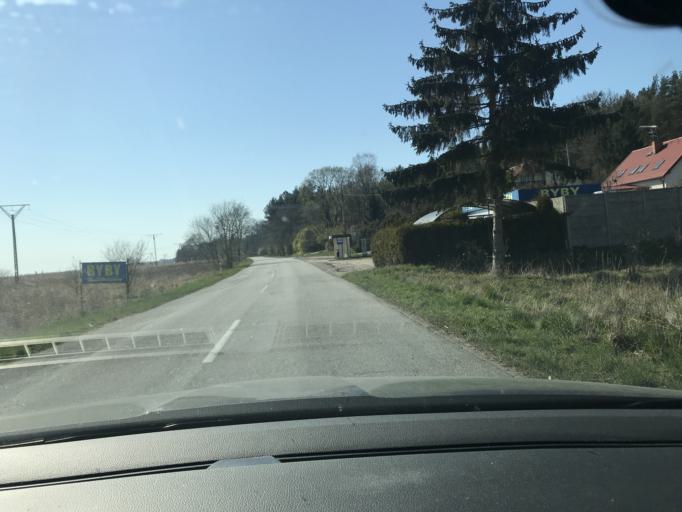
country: PL
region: Pomeranian Voivodeship
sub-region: Powiat nowodworski
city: Sztutowo
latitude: 54.3520
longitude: 19.2911
